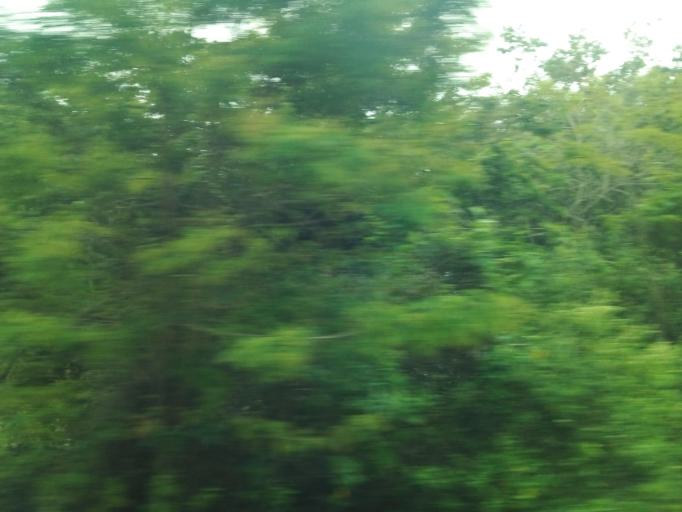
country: BR
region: Minas Gerais
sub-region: Nova Era
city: Nova Era
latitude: -19.7214
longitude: -42.9674
